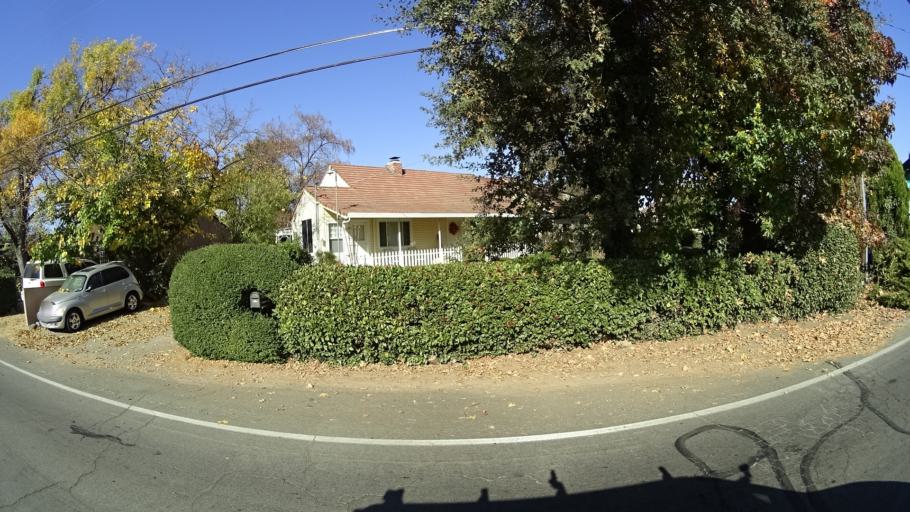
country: US
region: California
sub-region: Sacramento County
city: Citrus Heights
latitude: 38.7221
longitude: -121.2815
